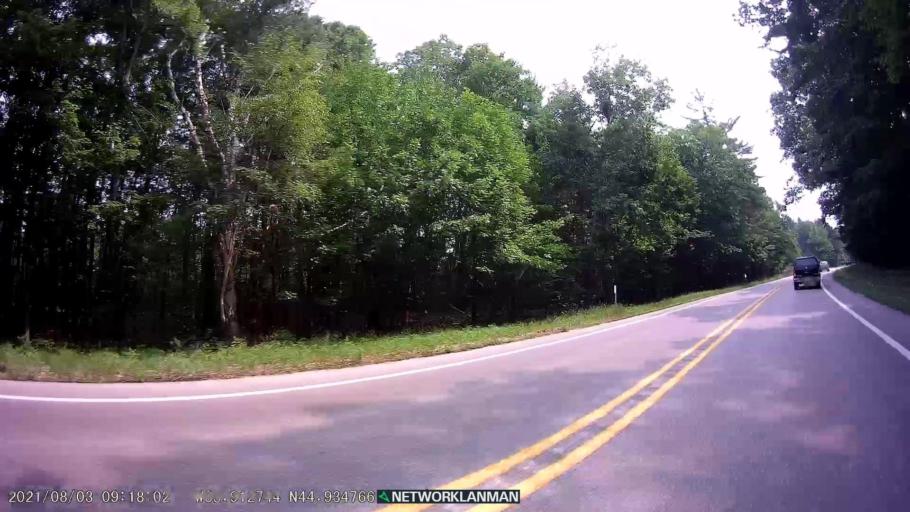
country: US
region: Michigan
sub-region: Leelanau County
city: Leland
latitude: 44.9346
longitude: -85.9119
